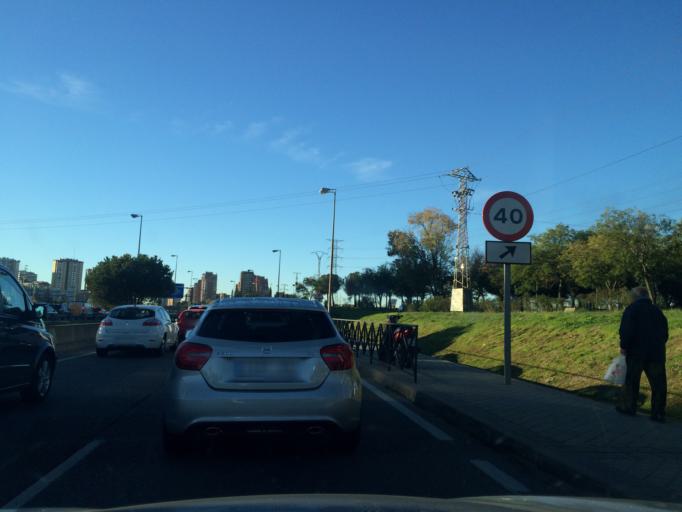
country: ES
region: Madrid
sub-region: Provincia de Madrid
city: Pinar de Chamartin
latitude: 40.4901
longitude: -3.6729
